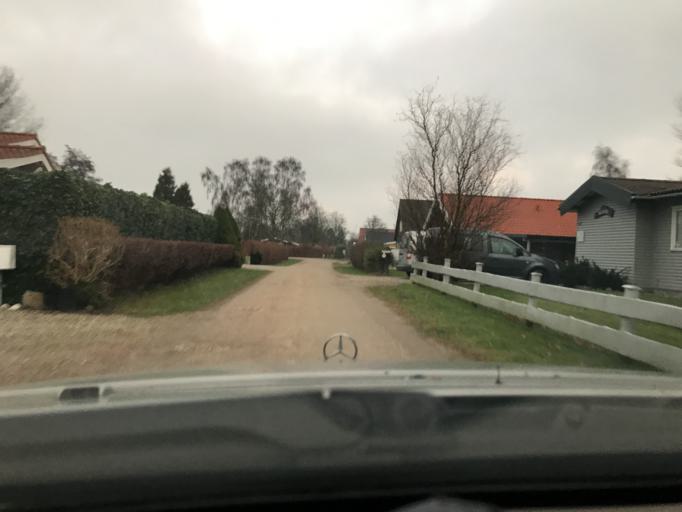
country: DK
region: South Denmark
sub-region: Sonderborg Kommune
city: Horuphav
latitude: 54.8733
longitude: 10.0196
